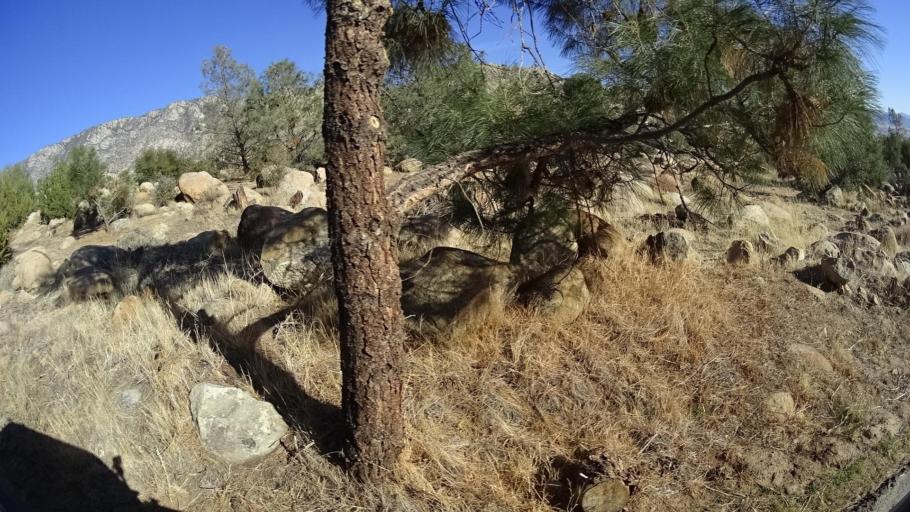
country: US
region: California
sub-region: Kern County
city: Weldon
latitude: 35.7155
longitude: -118.3057
